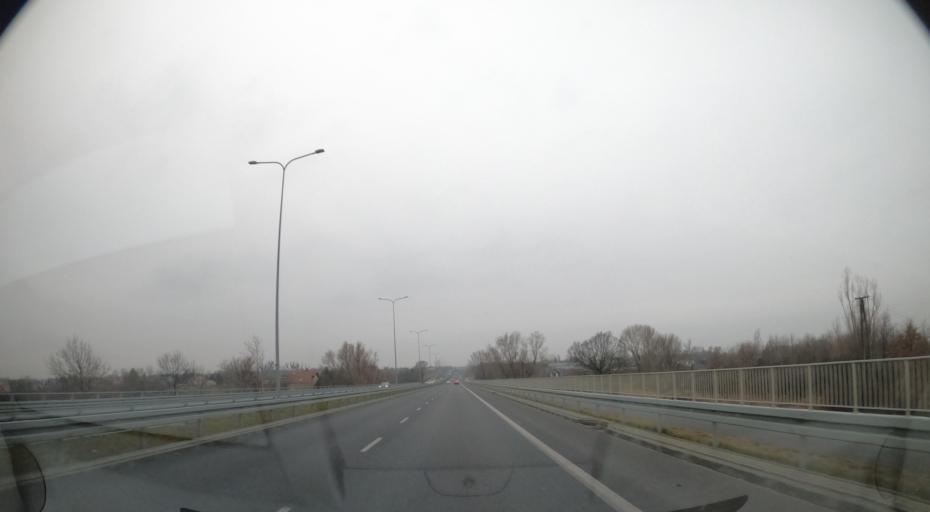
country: PL
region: Masovian Voivodeship
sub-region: Radom
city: Radom
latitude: 51.4060
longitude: 21.2019
